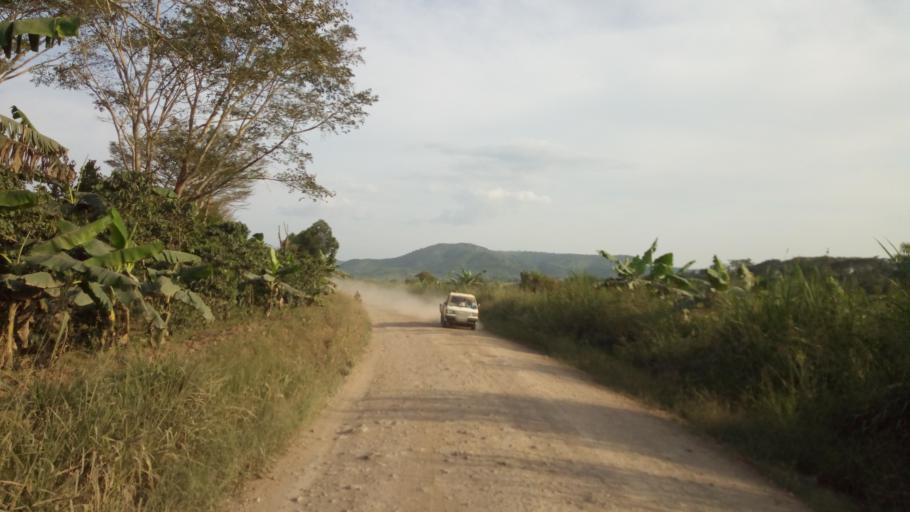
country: UG
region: Central Region
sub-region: Kiboga District
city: Kiboga
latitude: 0.7203
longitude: 31.7398
